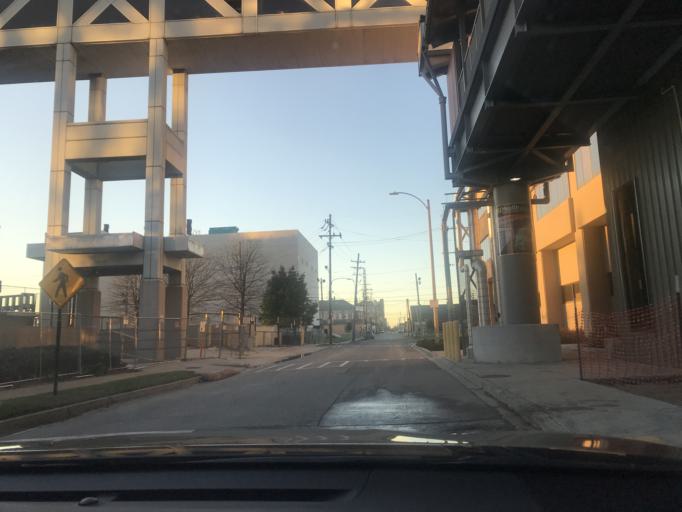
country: US
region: Louisiana
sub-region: Orleans Parish
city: New Orleans
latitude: 29.9573
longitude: -90.0843
